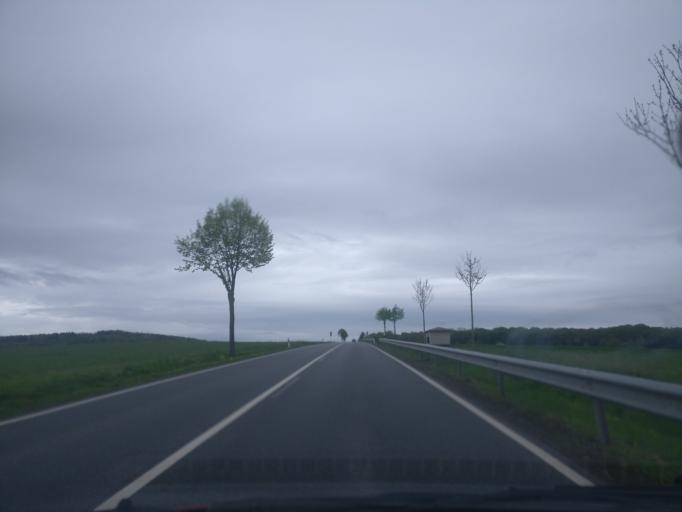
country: DE
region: Lower Saxony
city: Juhnde
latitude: 51.5143
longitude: 9.8078
